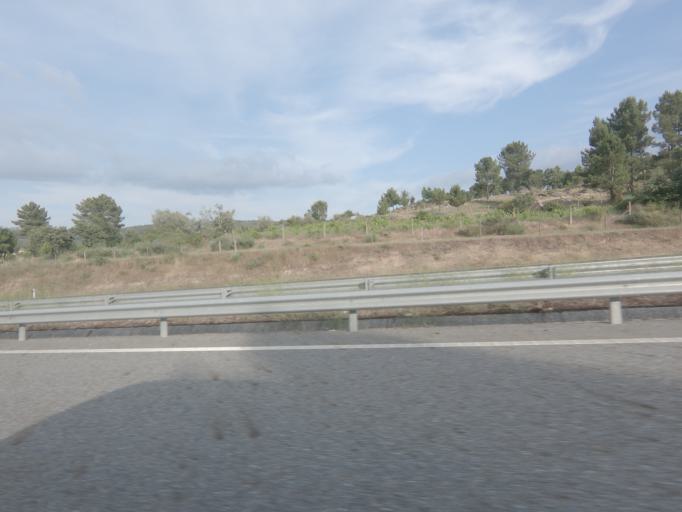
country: PT
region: Vila Real
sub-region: Boticas
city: Boticas
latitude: 41.6620
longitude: -7.5759
